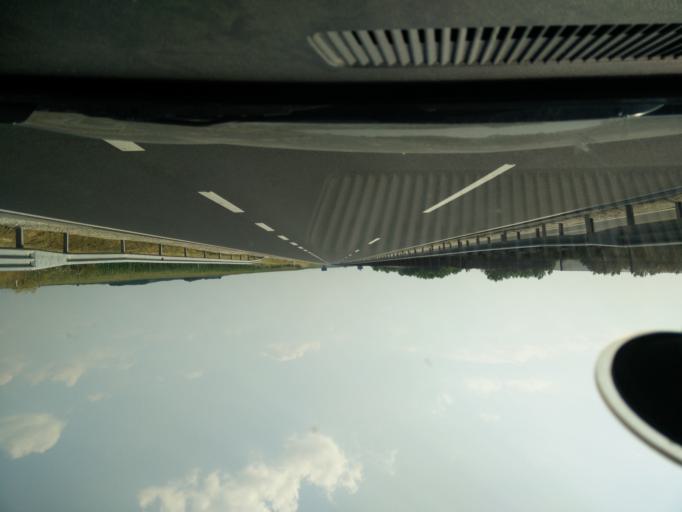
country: HU
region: Tolna
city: Tolna
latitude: 46.4145
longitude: 18.7339
